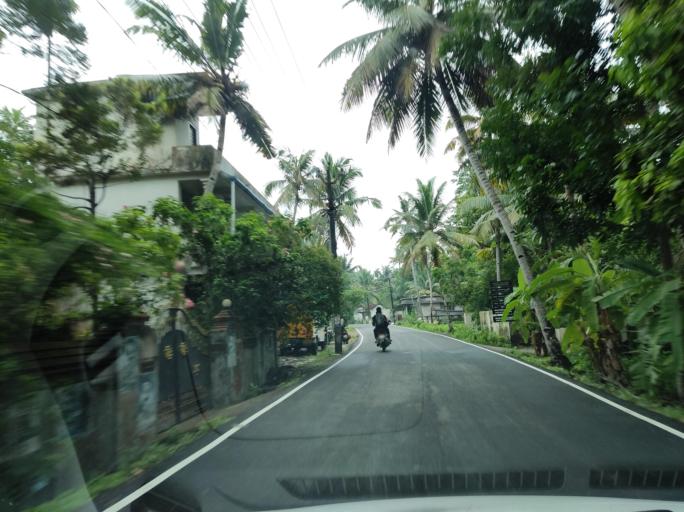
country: IN
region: Kerala
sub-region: Alappuzha
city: Kayankulam
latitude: 9.2736
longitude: 76.4017
